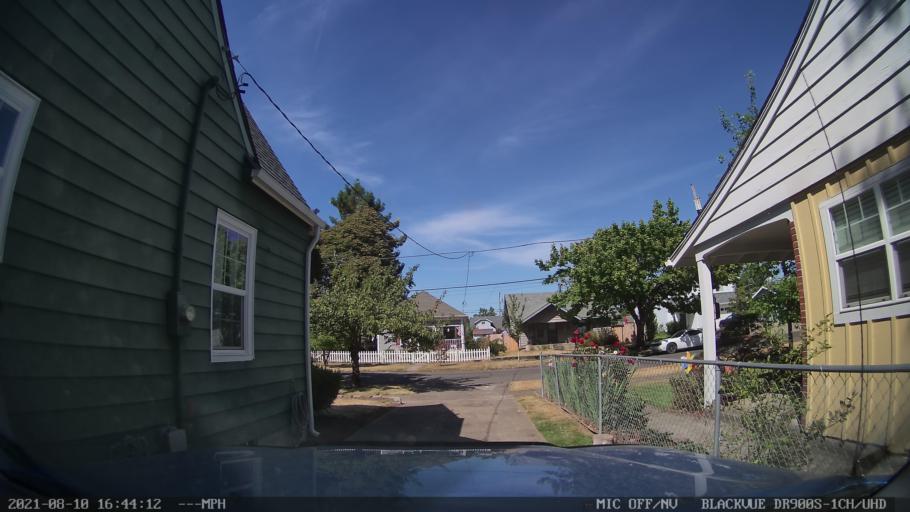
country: US
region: Oregon
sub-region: Marion County
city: Salem
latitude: 44.9534
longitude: -123.0221
